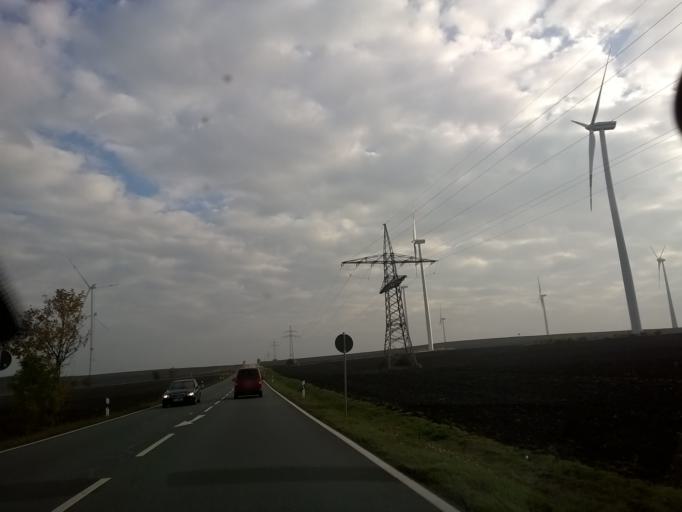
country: DE
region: Thuringia
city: Greussen
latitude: 51.2113
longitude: 10.9580
